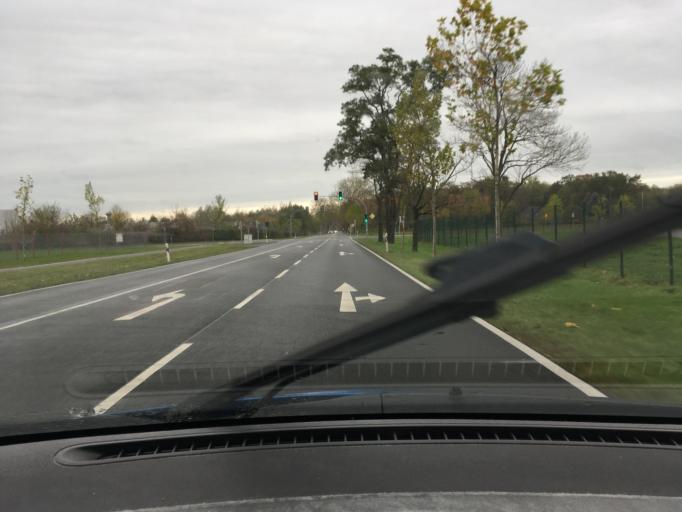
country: DE
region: Saxony-Anhalt
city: Rodleben
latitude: 51.9028
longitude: 12.2118
